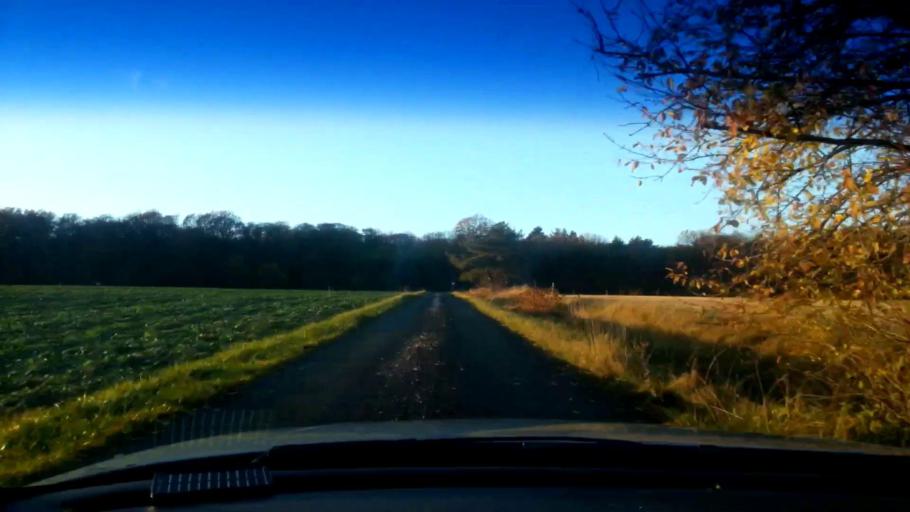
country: DE
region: Bavaria
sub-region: Upper Franconia
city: Buttenheim
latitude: 49.8223
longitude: 11.0488
